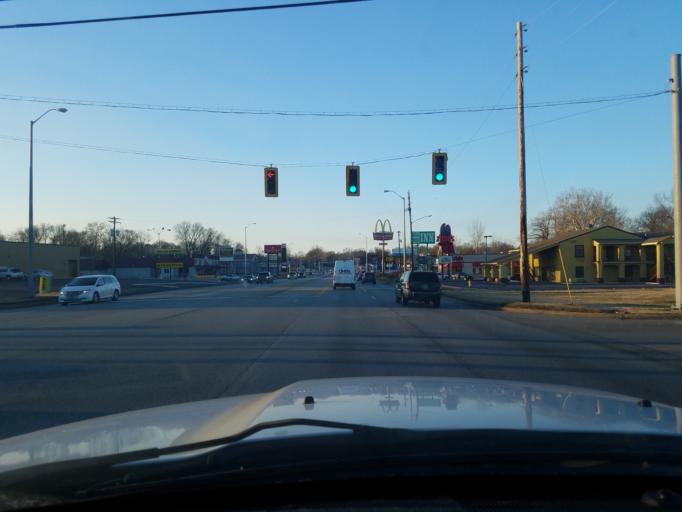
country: US
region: Kentucky
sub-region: Henderson County
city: Henderson
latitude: 37.8674
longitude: -87.5722
